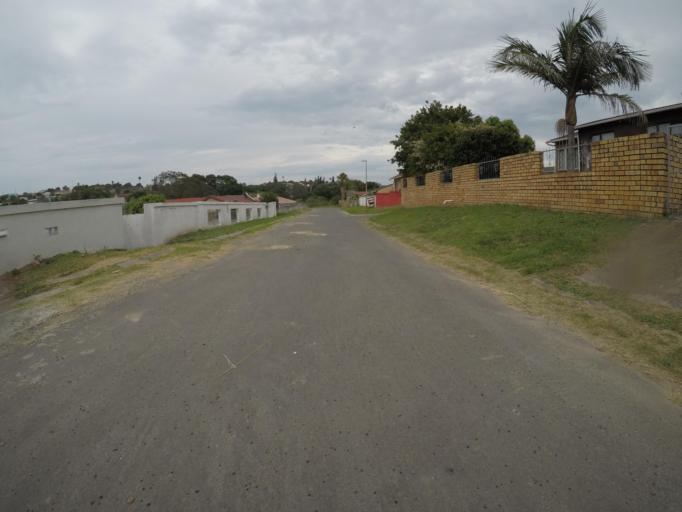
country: ZA
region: Eastern Cape
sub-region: Buffalo City Metropolitan Municipality
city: East London
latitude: -33.0006
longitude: 27.8592
